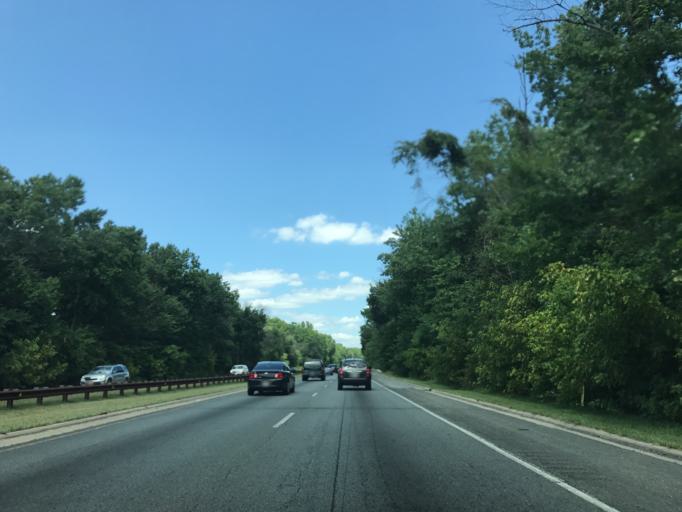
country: US
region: Maryland
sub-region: Prince George's County
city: South Laurel
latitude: 39.0671
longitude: -76.8328
